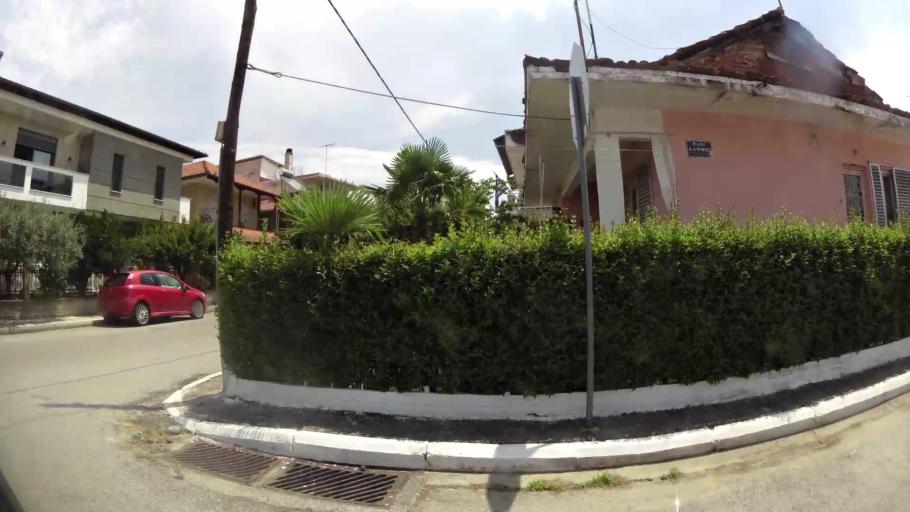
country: GR
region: Central Macedonia
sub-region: Nomos Pierias
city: Katerini
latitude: 40.2650
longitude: 22.5177
